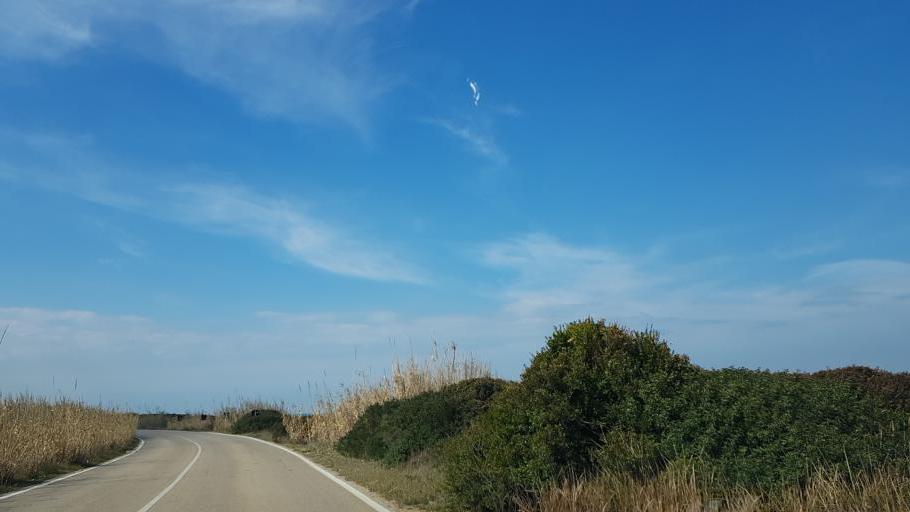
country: IT
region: Apulia
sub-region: Provincia di Brindisi
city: Brindisi
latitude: 40.6869
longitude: 17.8586
